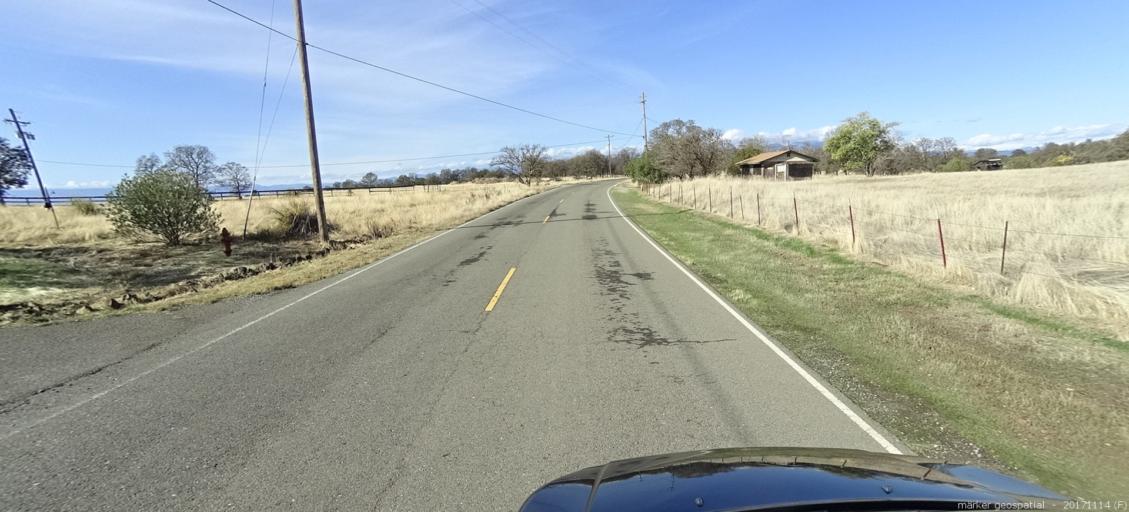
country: US
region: California
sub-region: Shasta County
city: Anderson
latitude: 40.4176
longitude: -122.3629
